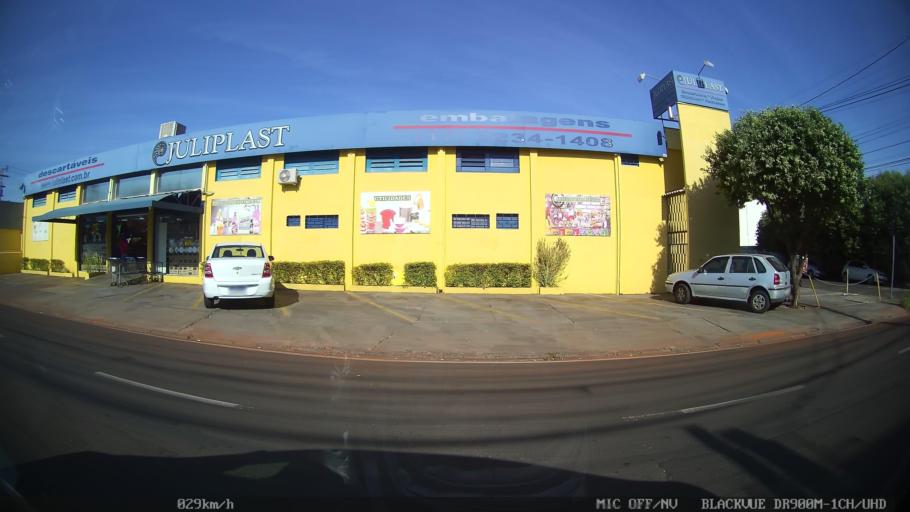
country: BR
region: Sao Paulo
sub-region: Sao Jose Do Rio Preto
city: Sao Jose do Rio Preto
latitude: -20.7990
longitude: -49.3674
